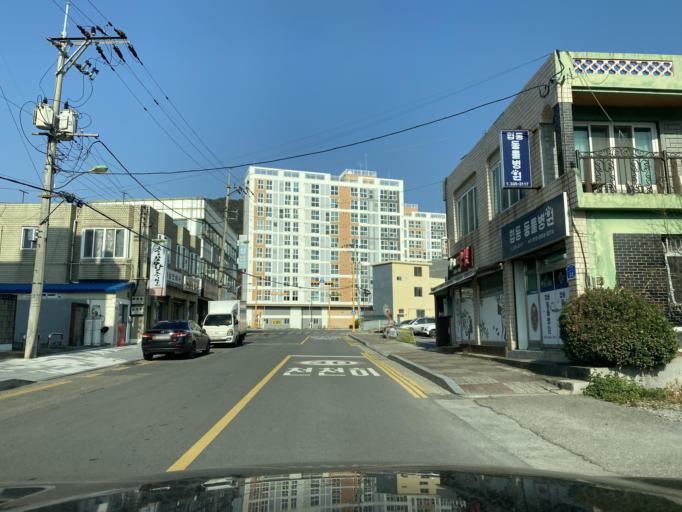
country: KR
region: Chungcheongnam-do
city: Yesan
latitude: 36.6815
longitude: 126.8483
